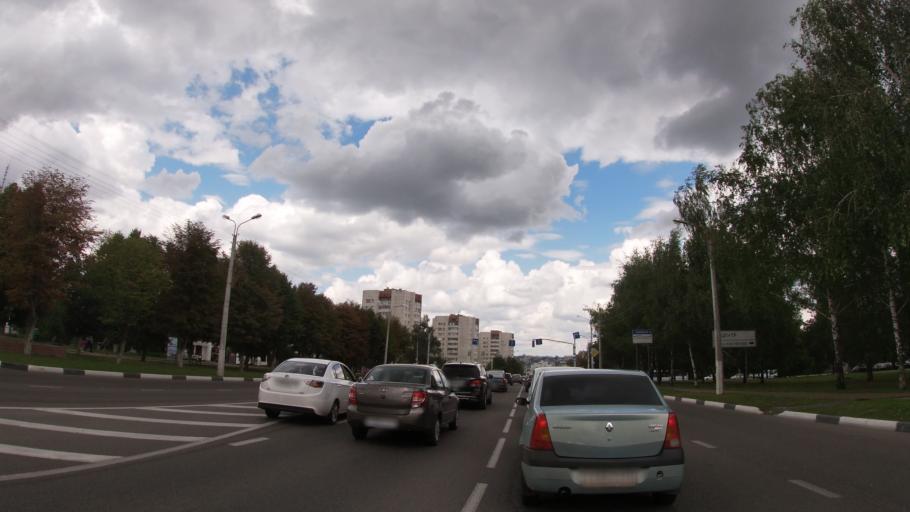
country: RU
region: Belgorod
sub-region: Belgorodskiy Rayon
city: Belgorod
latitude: 50.5777
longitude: 36.5828
